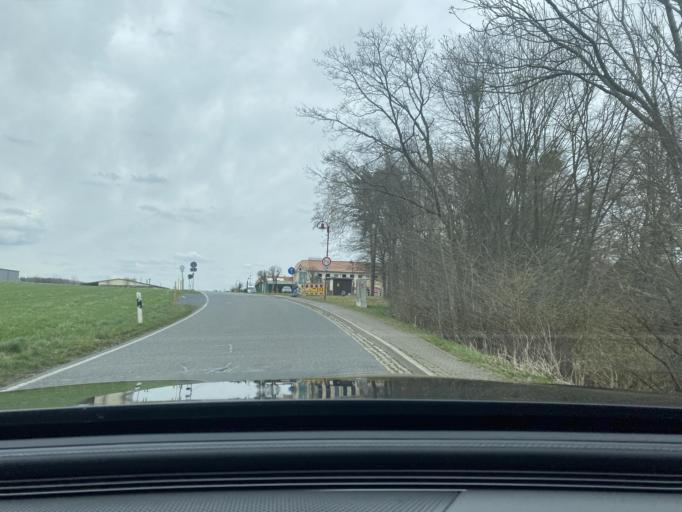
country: DE
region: Saxony
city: Durrrohrsdorf
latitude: 51.0253
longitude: 14.0097
